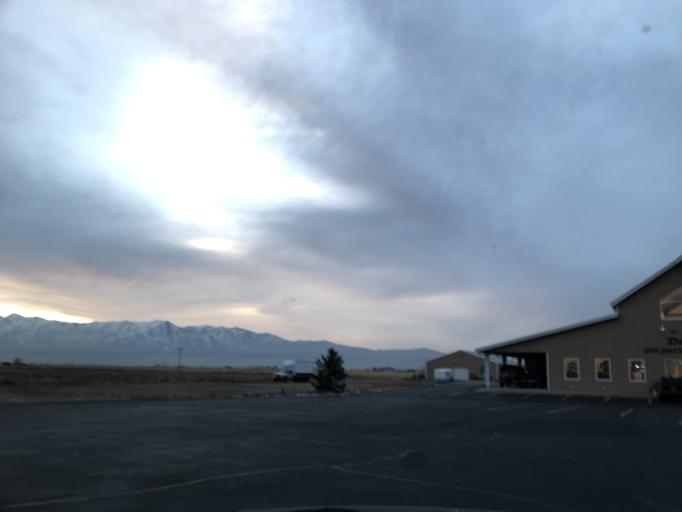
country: US
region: Utah
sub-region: Cache County
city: Benson
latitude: 41.7938
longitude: -111.8904
